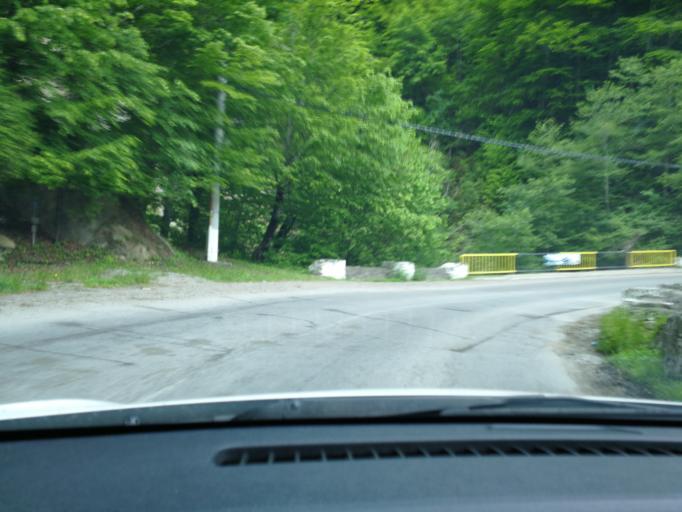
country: RO
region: Prahova
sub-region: Comuna Valea Doftanei
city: Tesila
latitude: 45.2763
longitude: 25.7322
